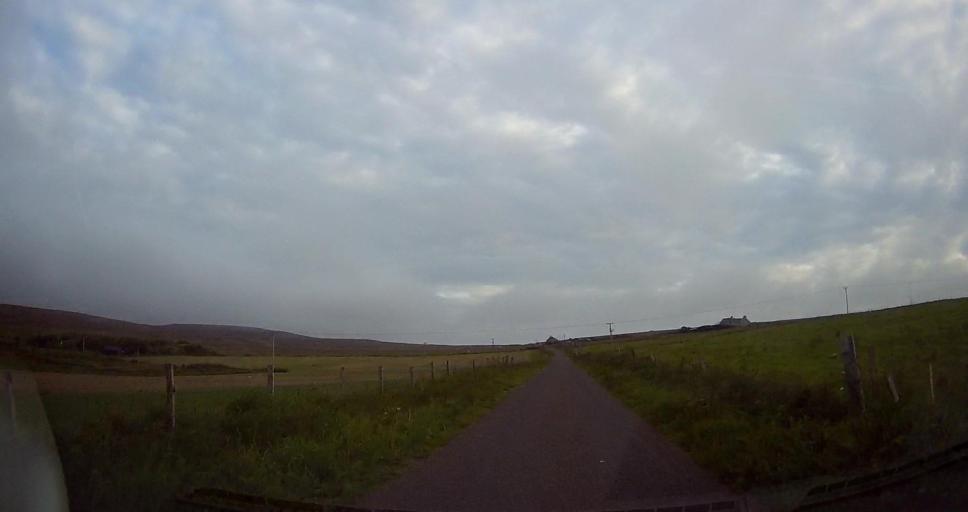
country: GB
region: Scotland
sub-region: Orkney Islands
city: Orkney
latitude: 59.1114
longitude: -3.1171
